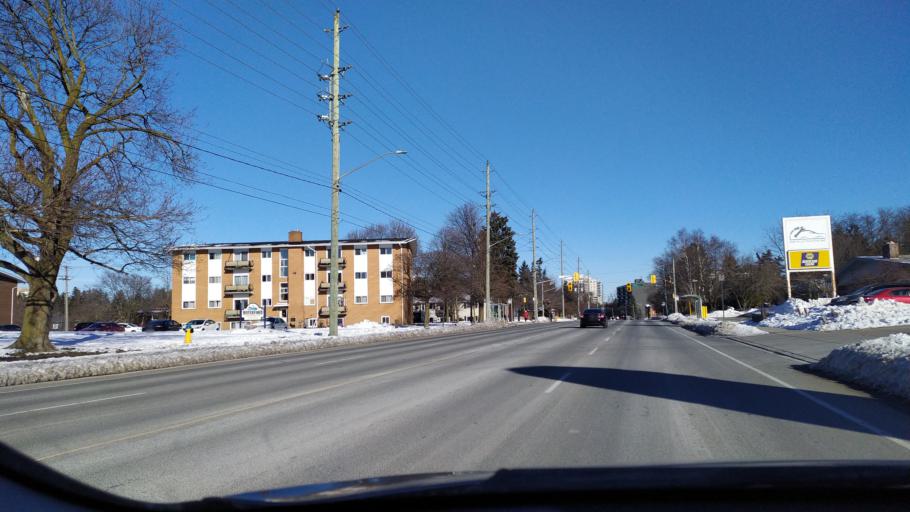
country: CA
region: Ontario
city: Waterloo
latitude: 43.4550
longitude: -80.5463
